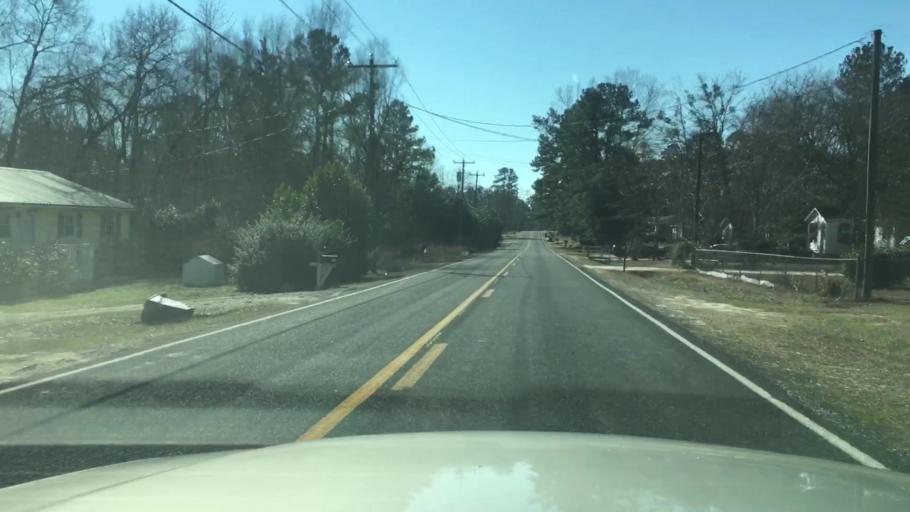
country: US
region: North Carolina
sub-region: Cumberland County
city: Hope Mills
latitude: 35.0012
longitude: -78.9646
